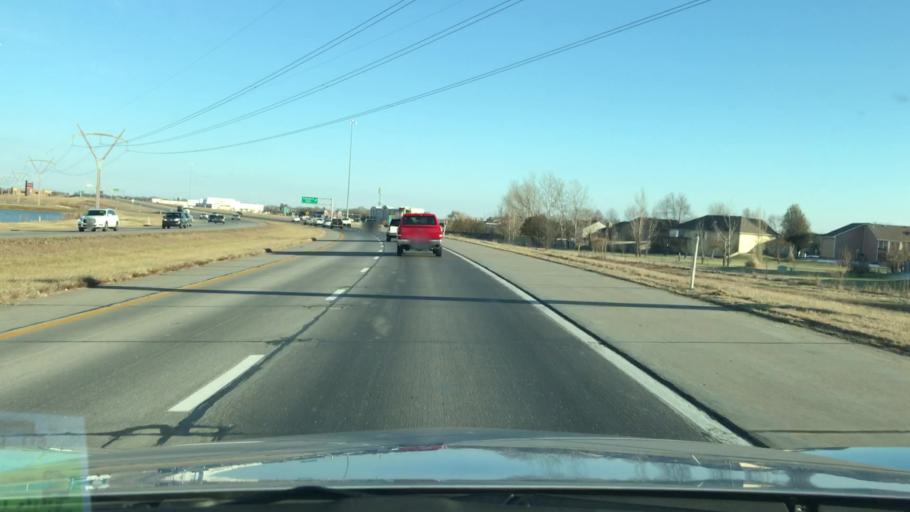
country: US
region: Kansas
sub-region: Sedgwick County
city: Bellaire
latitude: 37.7306
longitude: -97.2167
